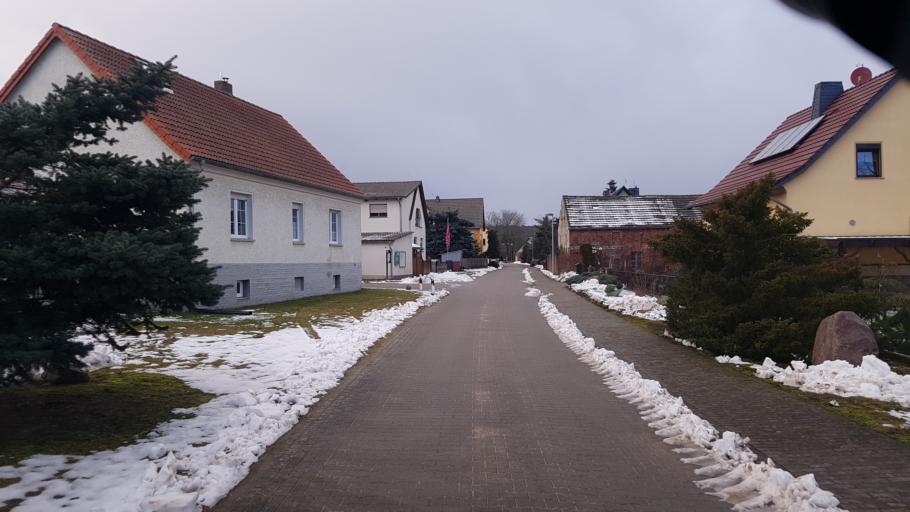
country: DE
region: Brandenburg
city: Schenkendobern
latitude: 51.8768
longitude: 14.6226
